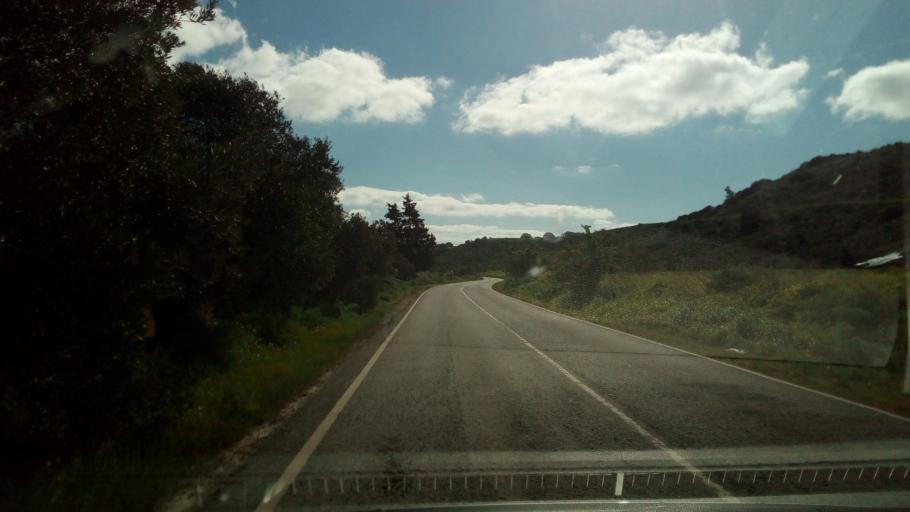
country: CY
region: Larnaka
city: Kofinou
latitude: 34.8049
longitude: 33.4700
